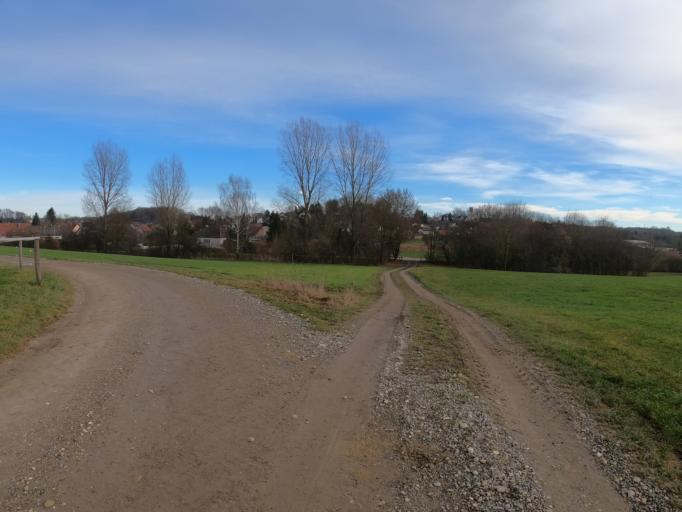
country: DE
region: Bavaria
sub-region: Swabia
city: Leipheim
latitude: 48.4180
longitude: 10.1790
